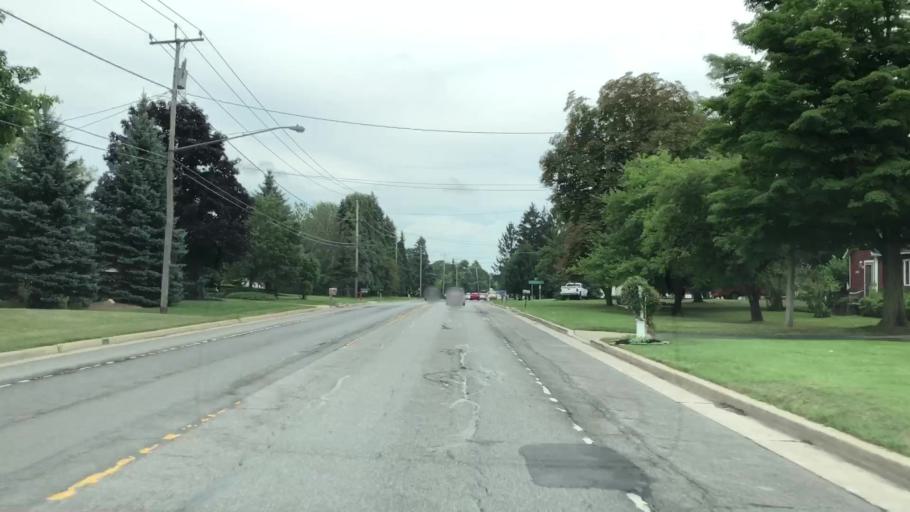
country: US
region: New York
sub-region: Erie County
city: Depew
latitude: 42.8877
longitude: -78.7087
